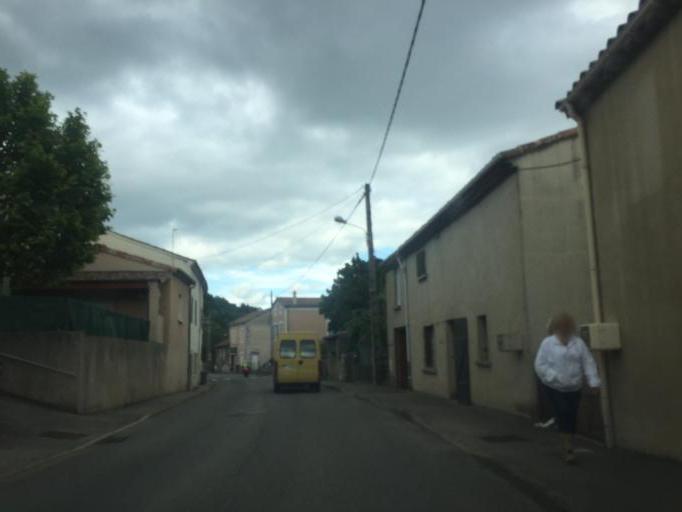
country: FR
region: Rhone-Alpes
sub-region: Departement de l'Ardeche
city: Privas
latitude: 44.7257
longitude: 4.5823
